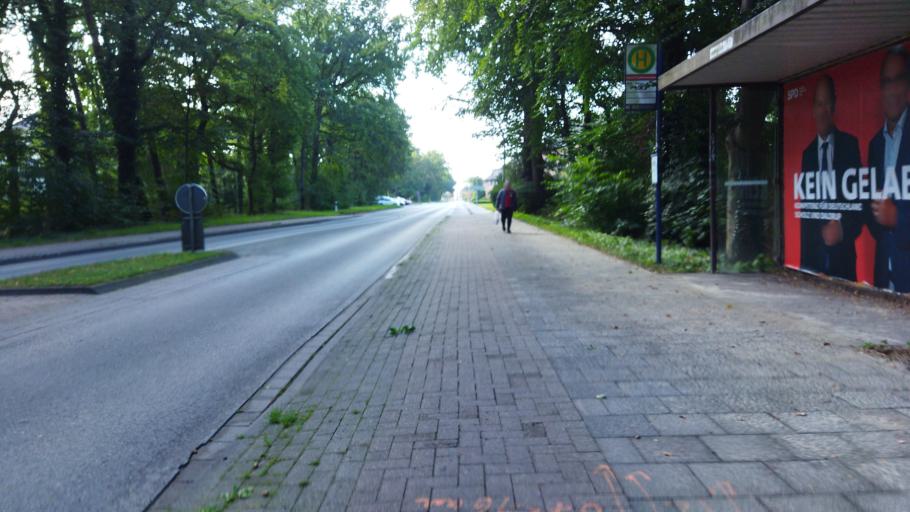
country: DE
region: North Rhine-Westphalia
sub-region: Regierungsbezirk Munster
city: Warendorf
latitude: 51.9682
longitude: 7.9934
